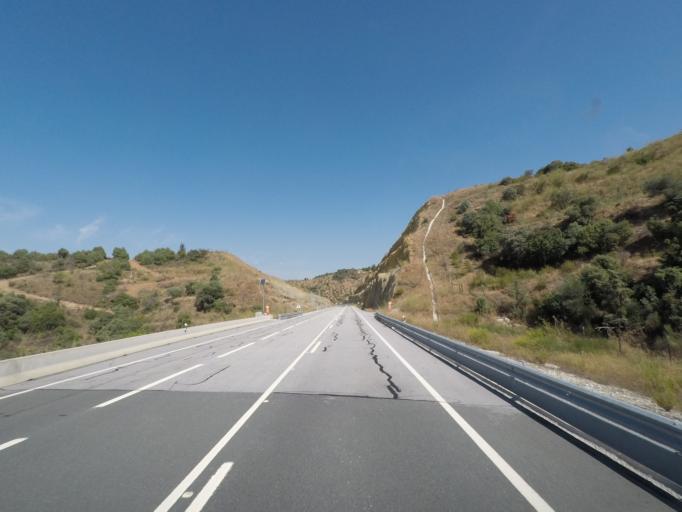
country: PT
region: Braganca
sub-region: Alfandega da Fe
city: Alfandega da Fe
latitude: 41.2905
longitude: -6.8958
